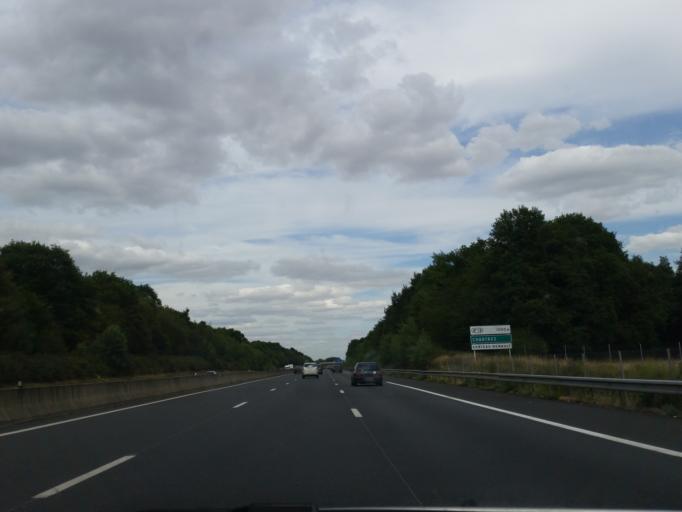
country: FR
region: Centre
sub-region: Departement d'Indre-et-Loire
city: Auzouer-en-Touraine
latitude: 47.5394
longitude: 0.9702
